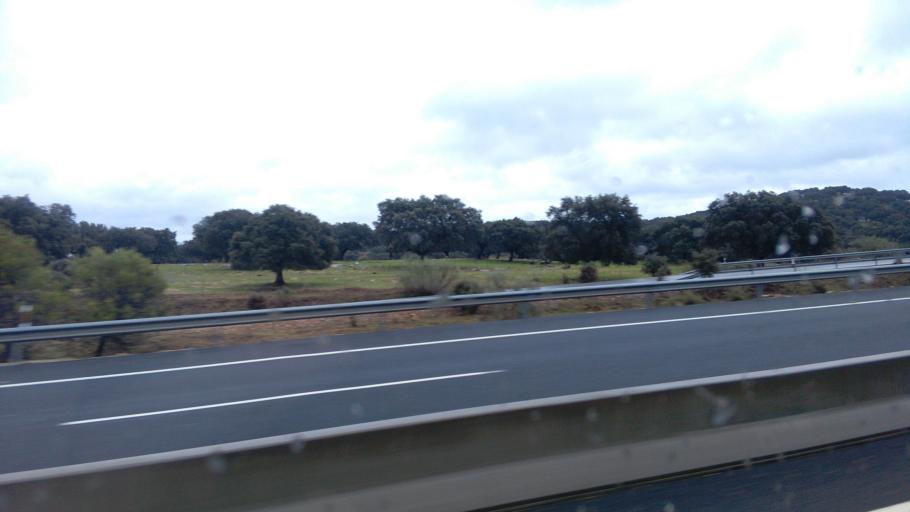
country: ES
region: Extremadura
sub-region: Provincia de Caceres
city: Casas de Miravete
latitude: 39.7649
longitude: -5.7344
